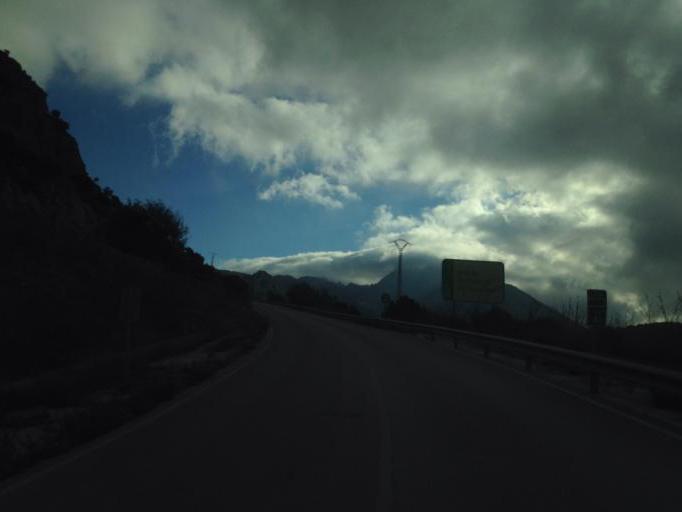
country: ES
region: Andalusia
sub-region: Provincia de Malaga
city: Casabermeja
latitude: 36.9561
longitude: -4.4371
